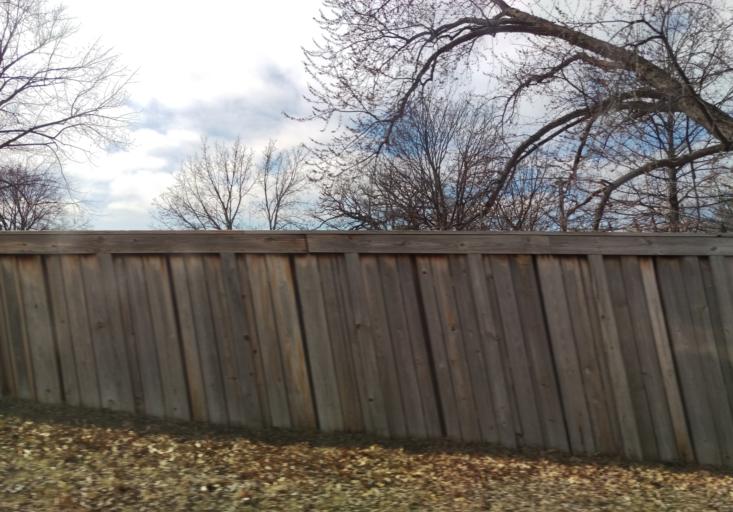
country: US
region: Minnesota
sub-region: Hennepin County
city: Minneapolis
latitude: 44.9228
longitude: -93.2212
